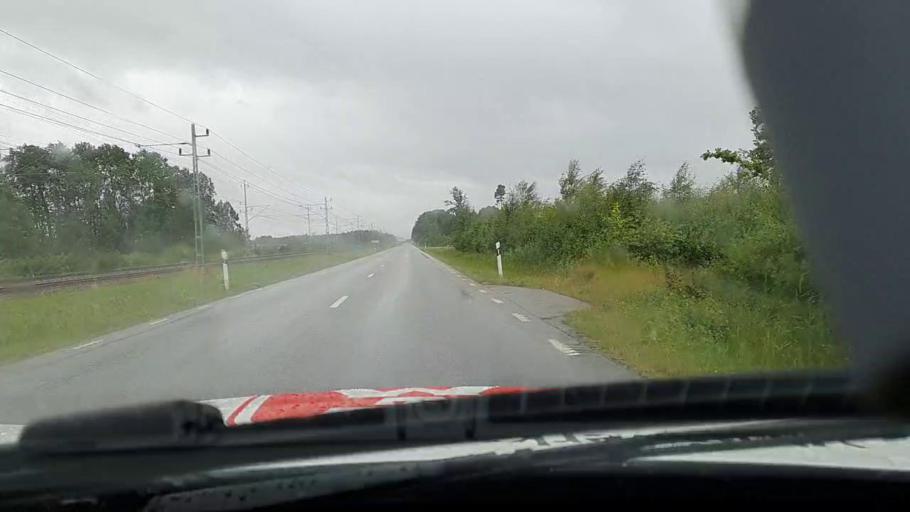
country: SE
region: Vaestra Goetaland
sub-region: Toreboda Kommun
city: Toereboda
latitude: 58.6819
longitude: 14.1064
